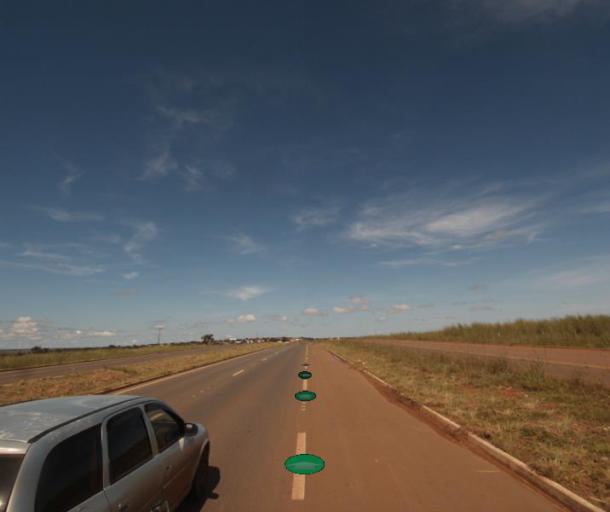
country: BR
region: Federal District
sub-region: Brasilia
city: Brasilia
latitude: -15.7443
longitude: -48.3177
